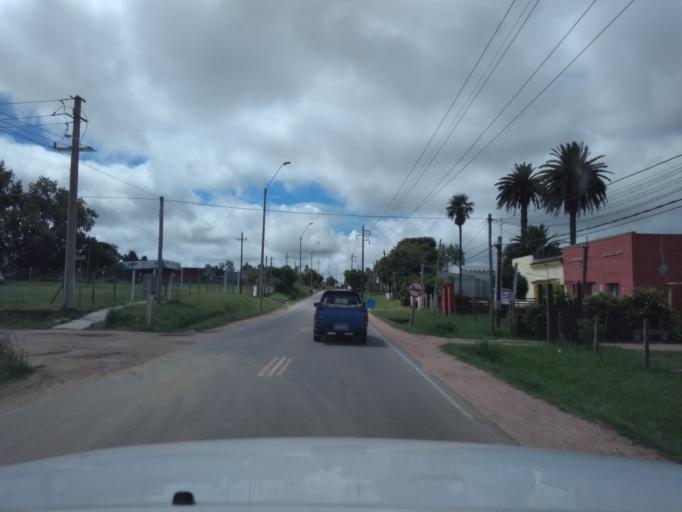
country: UY
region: Canelones
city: Pando
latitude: -34.7074
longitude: -55.9650
